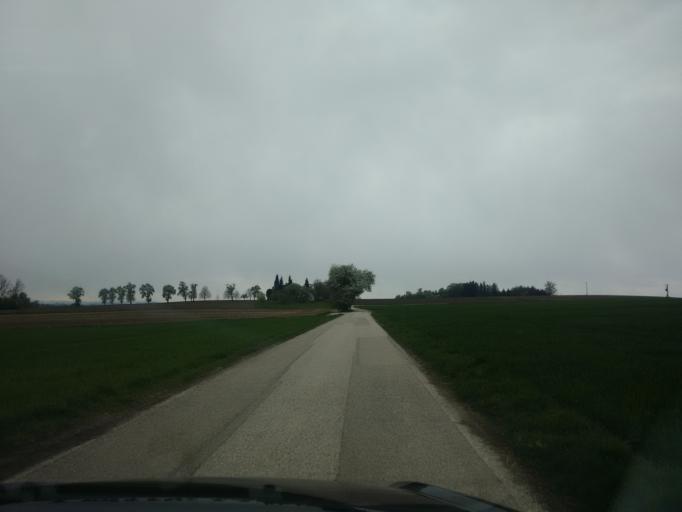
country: AT
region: Upper Austria
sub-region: Wels-Land
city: Buchkirchen
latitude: 48.2105
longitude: 14.0200
